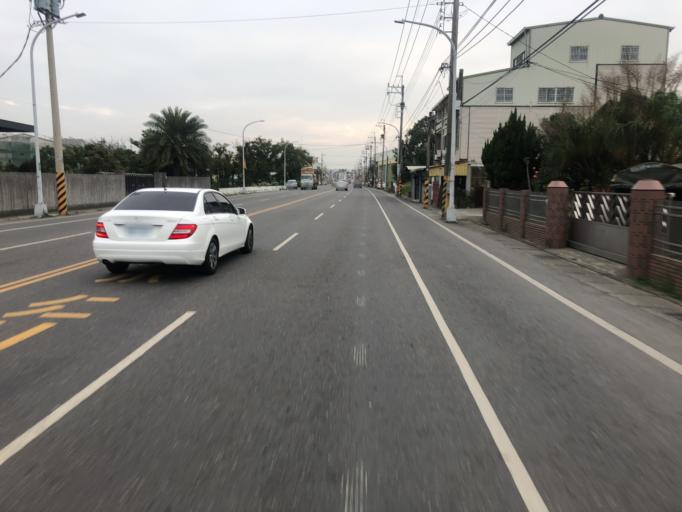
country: TW
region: Taiwan
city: Xinying
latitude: 23.1439
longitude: 120.2881
